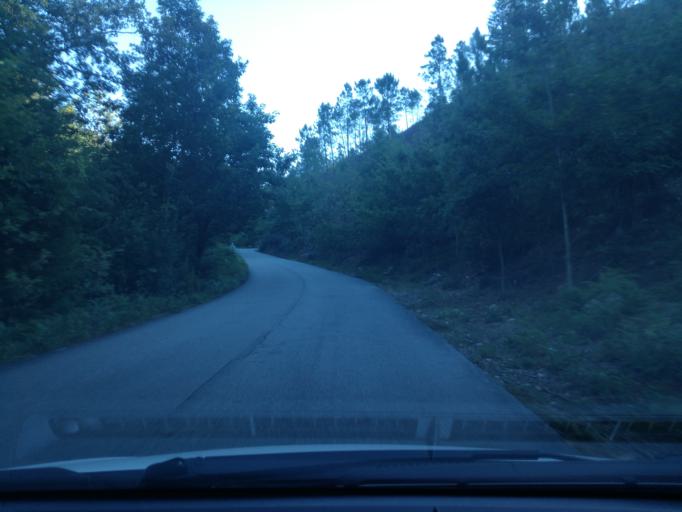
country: PT
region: Braga
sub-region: Vieira do Minho
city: Real
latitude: 41.7394
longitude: -8.1565
